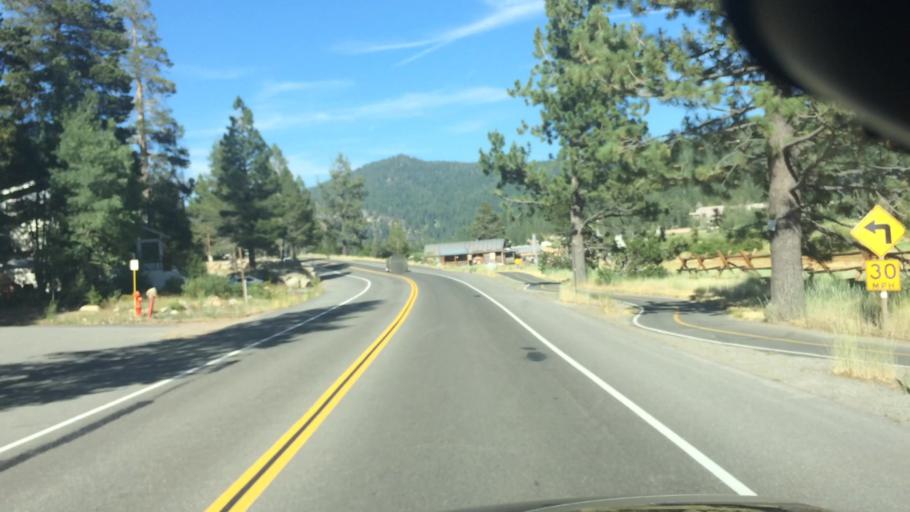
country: US
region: California
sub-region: Placer County
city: Sunnyside-Tahoe City
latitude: 39.1996
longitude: -120.2272
